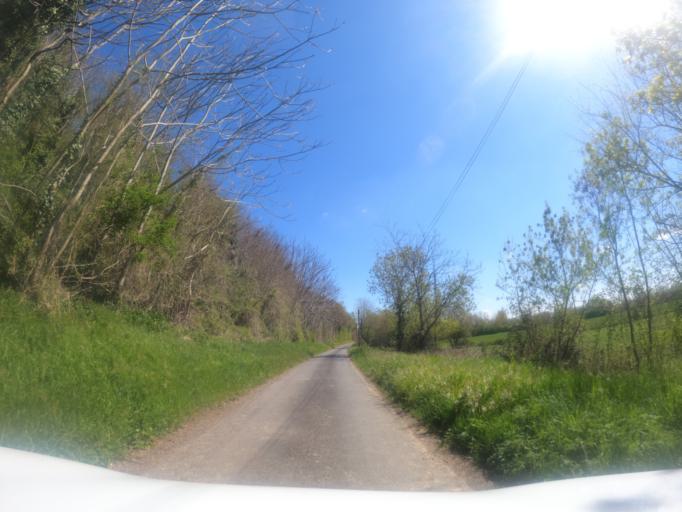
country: FR
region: Pays de la Loire
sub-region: Departement de la Vendee
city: Le Langon
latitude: 46.4361
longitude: -0.8810
